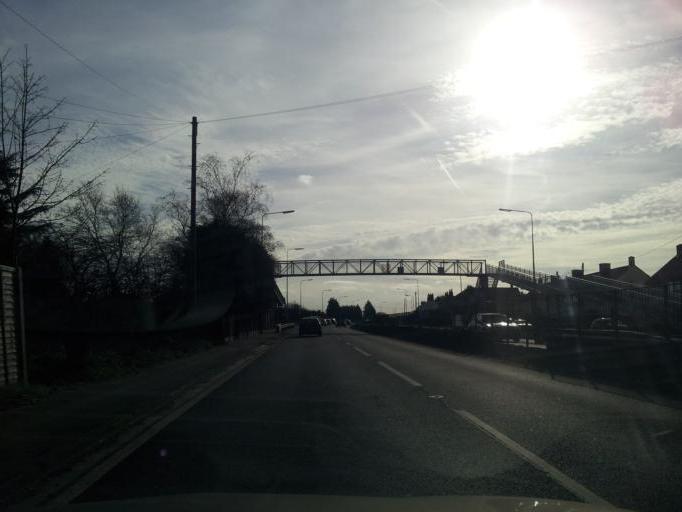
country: GB
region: England
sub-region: Central Bedfordshire
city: Sandy
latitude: 52.1212
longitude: -0.2938
